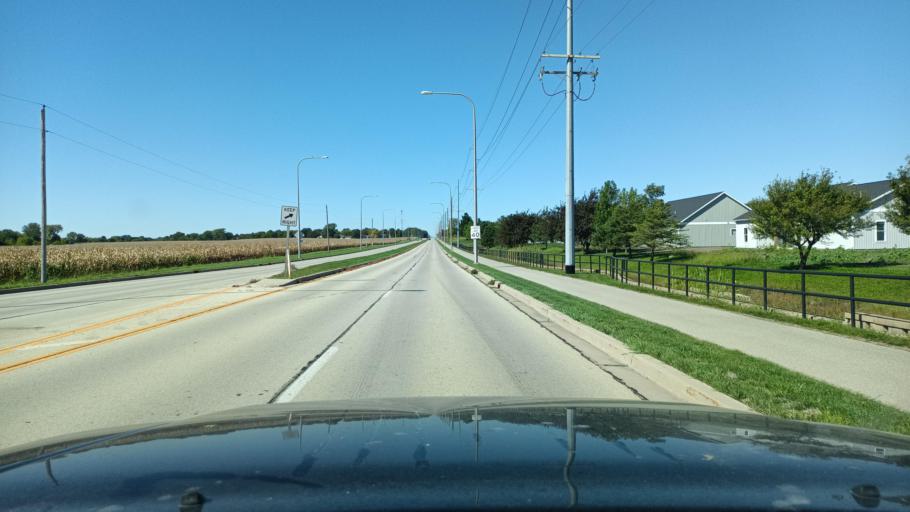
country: US
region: Illinois
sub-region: Champaign County
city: Urbana
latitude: 40.0840
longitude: -88.1696
